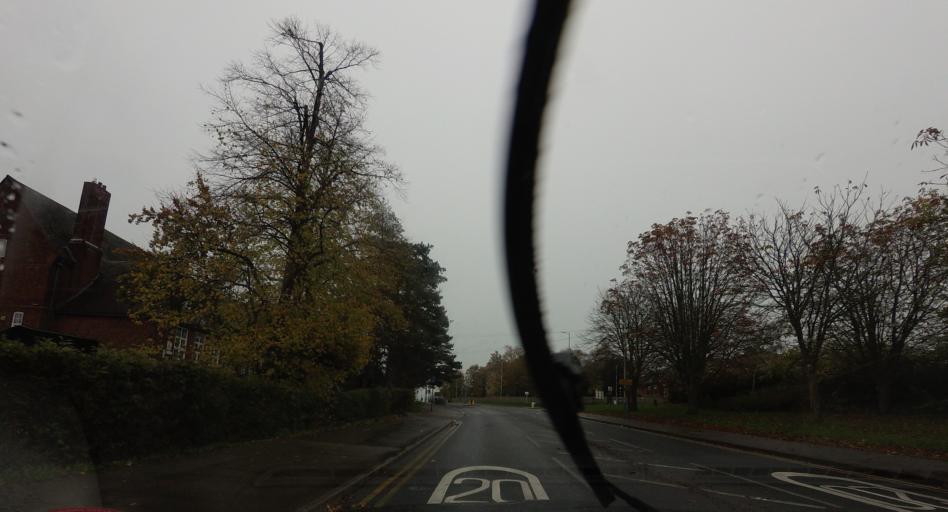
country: GB
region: England
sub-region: Kent
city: Tonbridge
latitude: 51.1877
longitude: 0.2636
